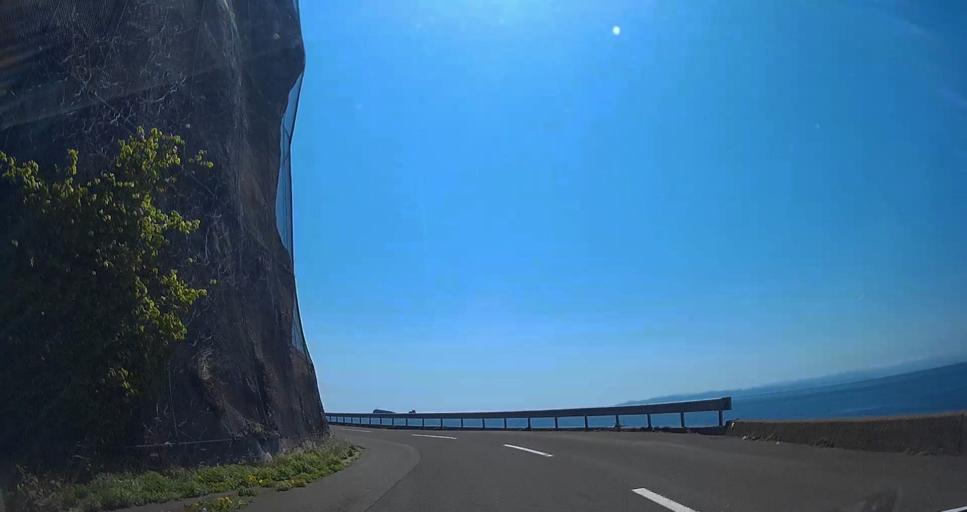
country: JP
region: Aomori
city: Aomori Shi
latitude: 41.1316
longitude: 140.7831
